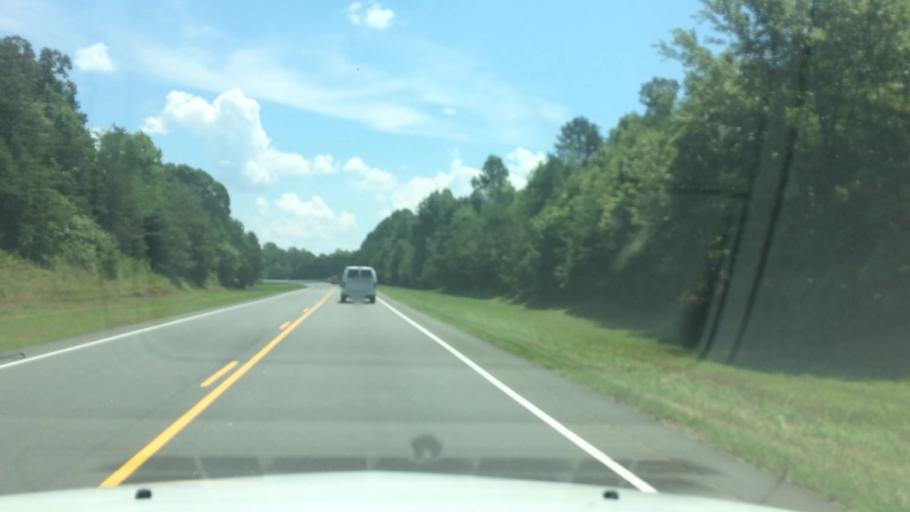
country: US
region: North Carolina
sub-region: Alexander County
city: Stony Point
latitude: 35.8279
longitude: -81.0141
